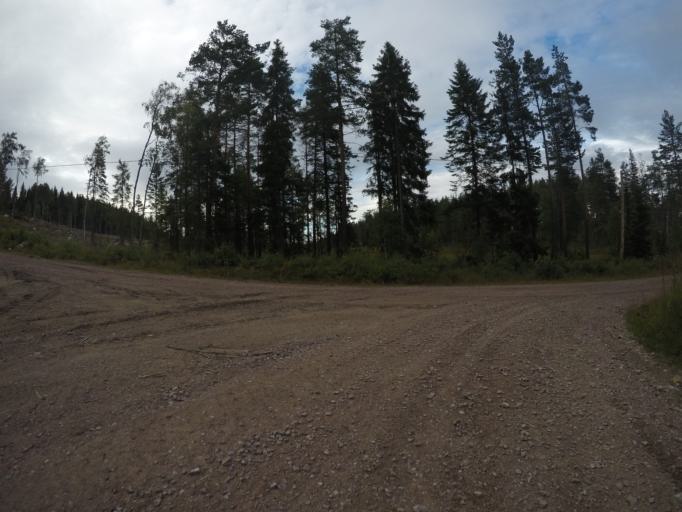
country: SE
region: OErebro
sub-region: Hallefors Kommun
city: Haellefors
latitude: 60.0377
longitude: 14.4690
